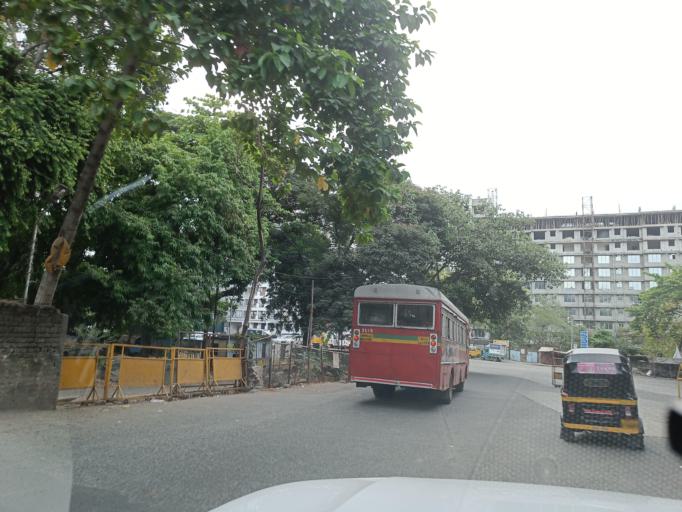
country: IN
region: Maharashtra
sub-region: Mumbai Suburban
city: Powai
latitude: 19.0913
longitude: 72.9070
